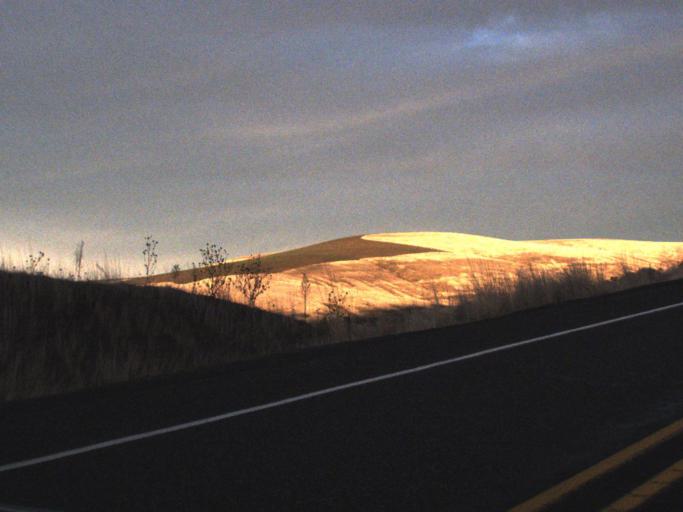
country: US
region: Washington
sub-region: Garfield County
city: Pomeroy
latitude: 46.5866
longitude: -117.7809
